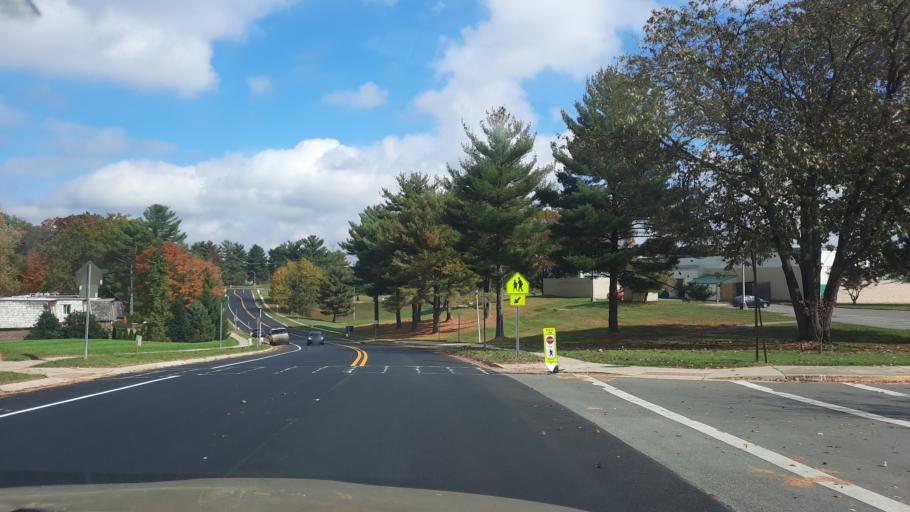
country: US
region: Maryland
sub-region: Montgomery County
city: Montgomery Village
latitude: 39.1744
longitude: -77.2127
